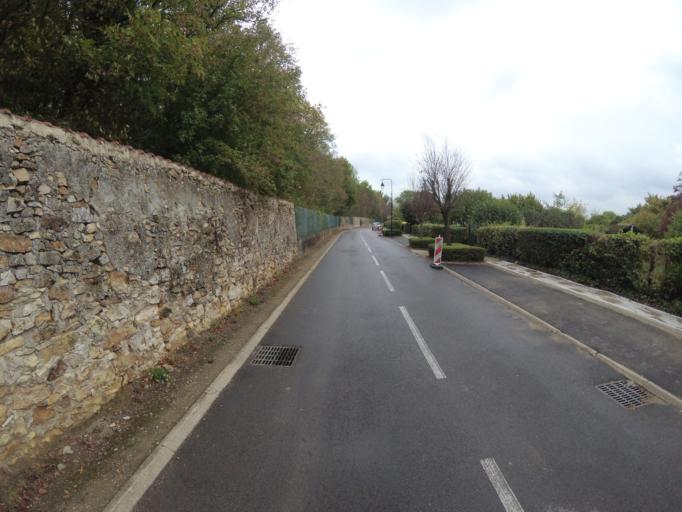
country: FR
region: Ile-de-France
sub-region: Departement de Seine-et-Marne
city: Bussy-Saint-Georges
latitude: 48.8480
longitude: 2.6940
